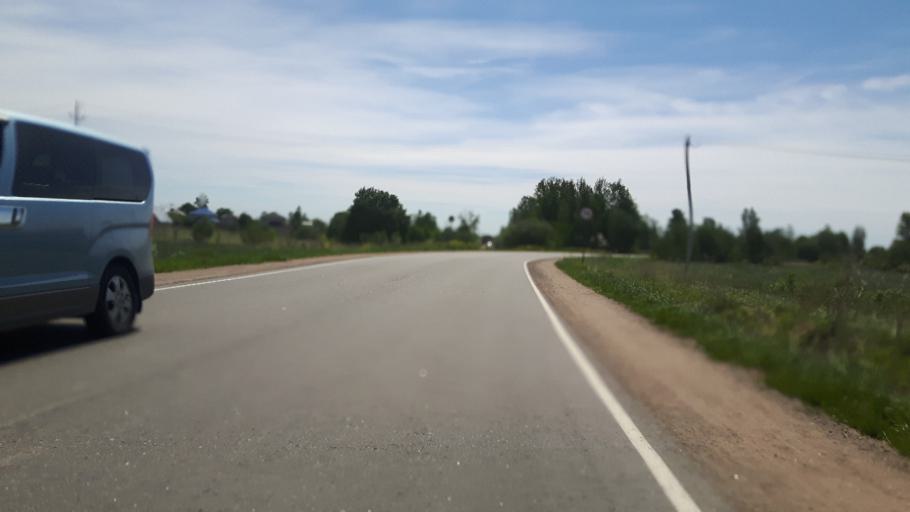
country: RU
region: Leningrad
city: Ust'-Luga
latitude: 59.5728
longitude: 28.1718
